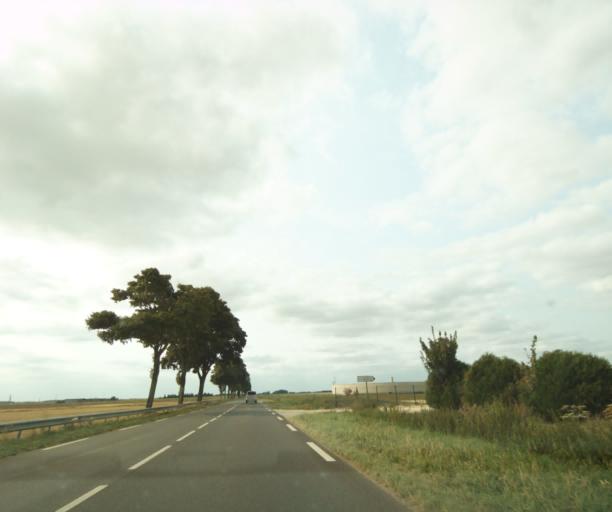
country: FR
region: Centre
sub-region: Departement d'Indre-et-Loire
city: Reignac-sur-Indre
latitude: 47.1982
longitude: 0.9161
